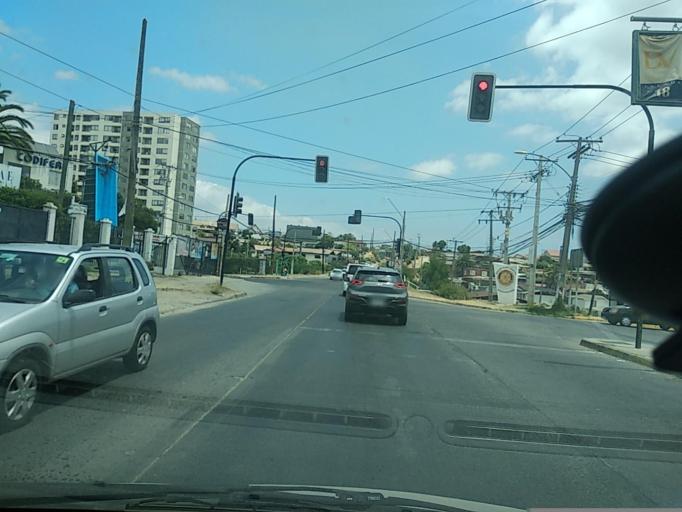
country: CL
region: Valparaiso
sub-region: Provincia de Marga Marga
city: Quilpue
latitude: -33.0422
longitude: -71.4270
